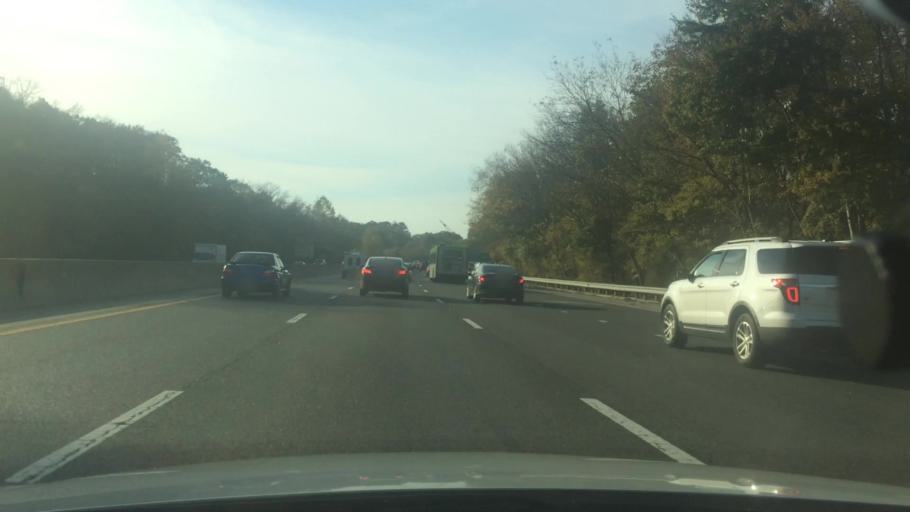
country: US
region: North Carolina
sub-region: Orange County
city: Chapel Hill
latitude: 35.9039
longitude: -78.9661
